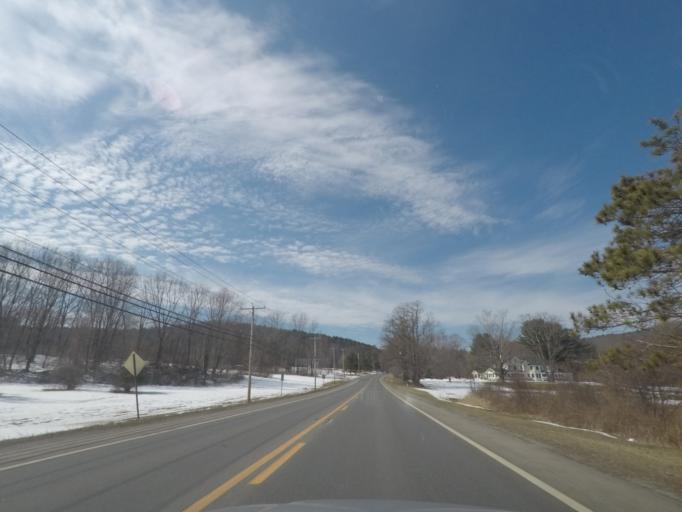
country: US
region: Massachusetts
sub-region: Berkshire County
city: Stockbridge
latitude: 42.3028
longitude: -73.3412
